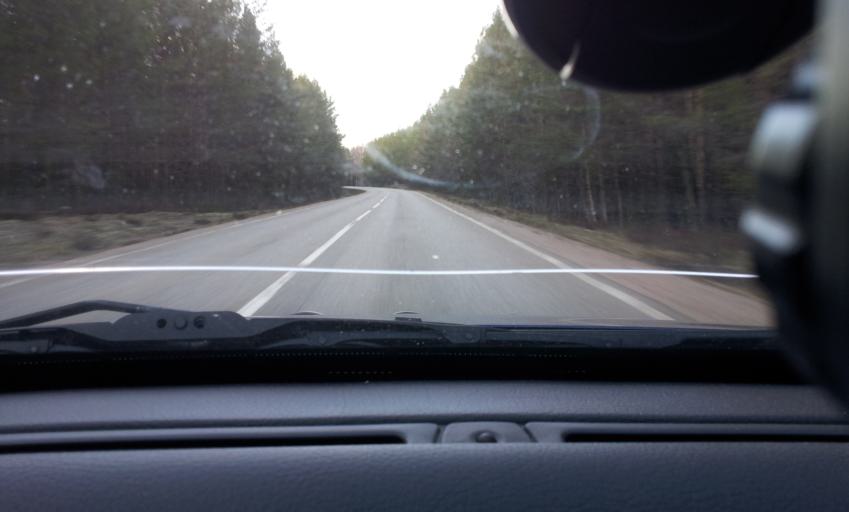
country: SE
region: Vaesternorrland
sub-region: Ange Kommun
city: Ange
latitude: 62.0859
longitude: 15.0946
